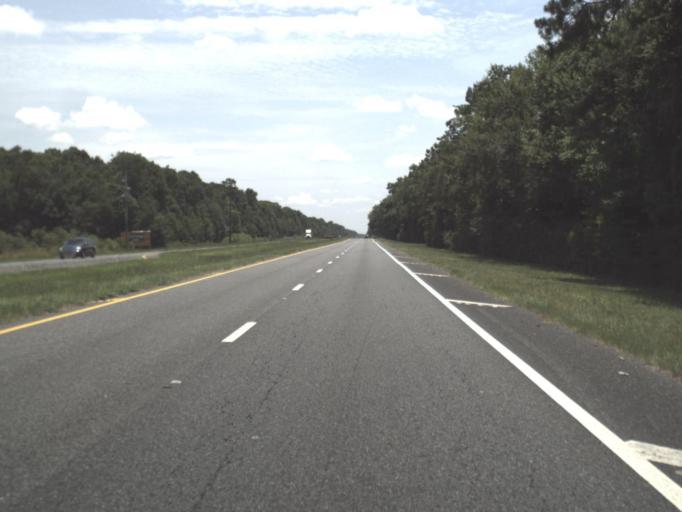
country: US
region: Florida
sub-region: Dixie County
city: Cross City
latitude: 29.6724
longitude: -83.2343
